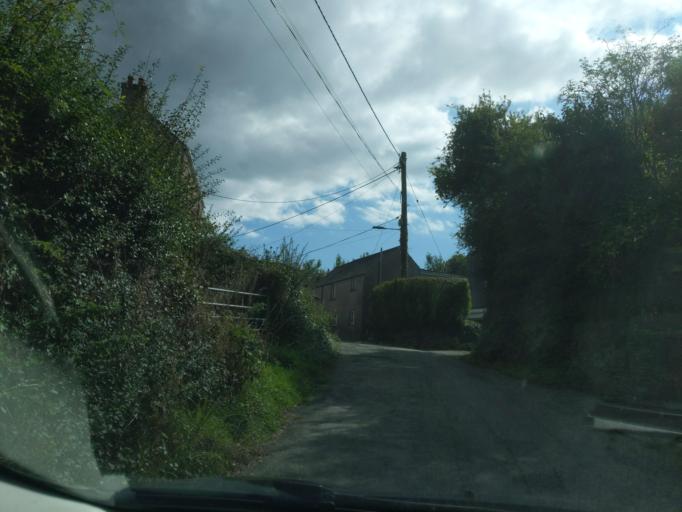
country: GB
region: England
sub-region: Plymouth
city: Plymstock
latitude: 50.3435
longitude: -4.0910
